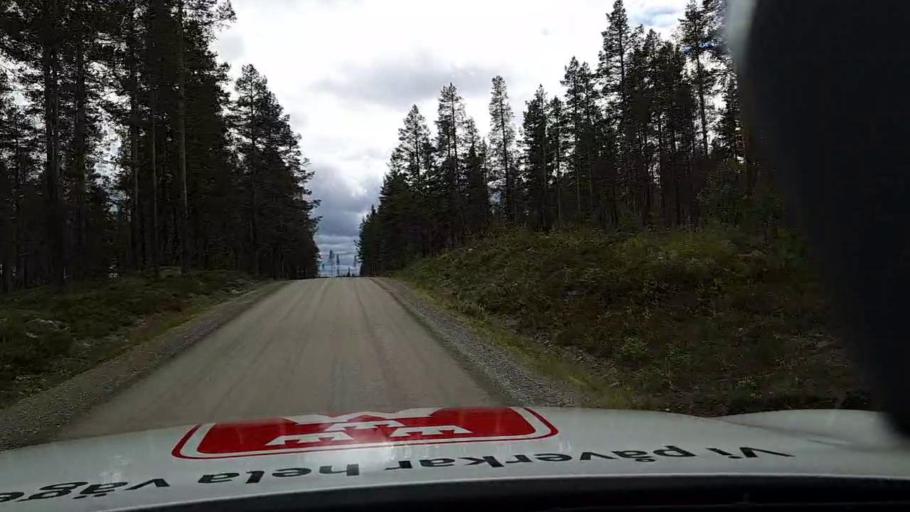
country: SE
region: Jaemtland
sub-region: Are Kommun
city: Jarpen
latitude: 62.8165
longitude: 13.8093
